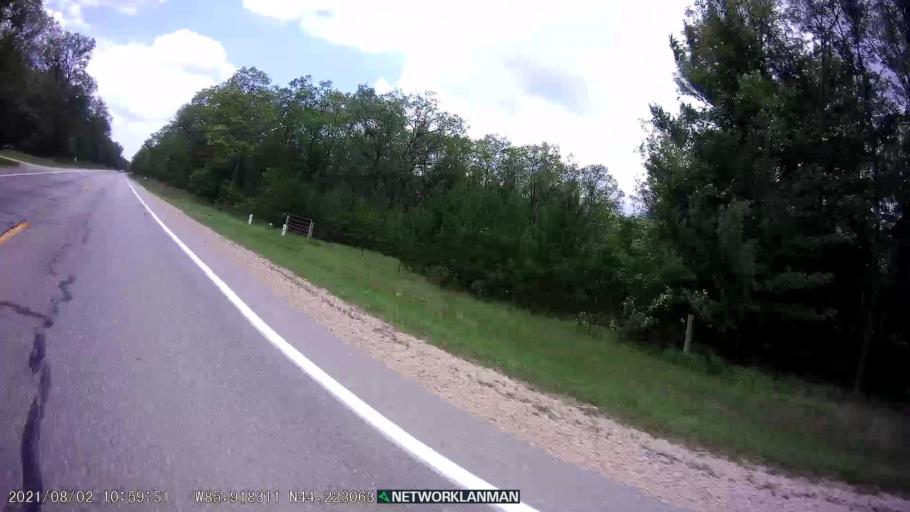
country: US
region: Michigan
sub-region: Lake County
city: Baldwin
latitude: 44.2230
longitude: -85.9189
